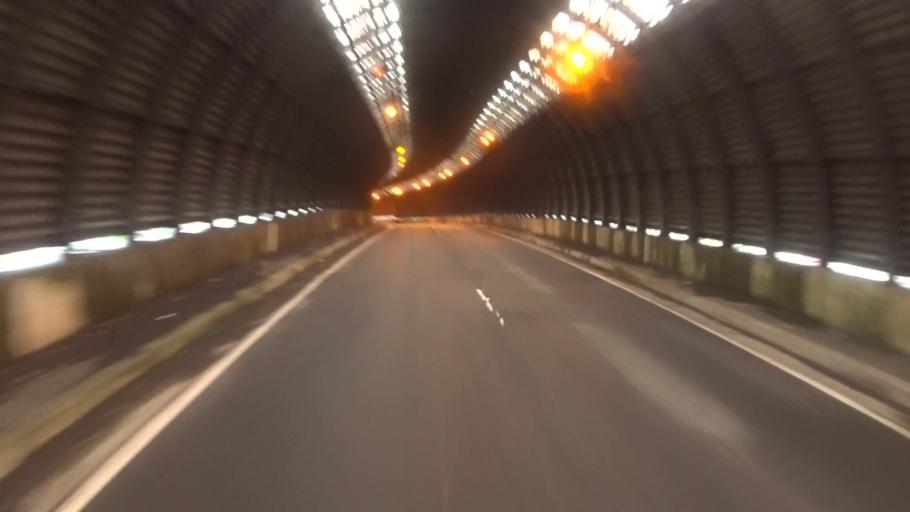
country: JP
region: Kyoto
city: Miyazu
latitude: 35.5275
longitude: 135.0404
